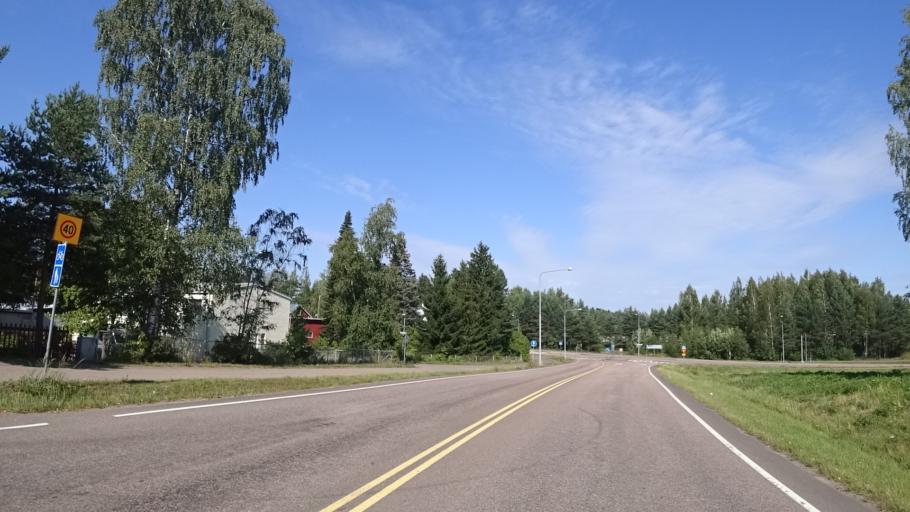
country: FI
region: Kymenlaakso
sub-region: Kotka-Hamina
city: Hamina
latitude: 60.5625
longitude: 27.1589
